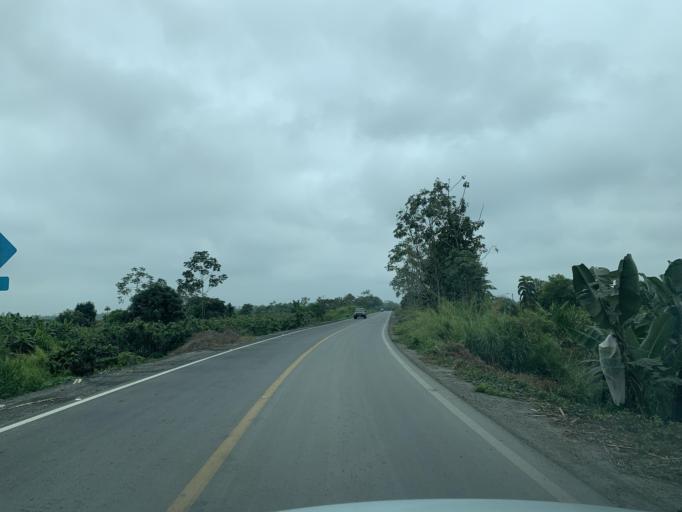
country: EC
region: Guayas
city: Coronel Marcelino Mariduena
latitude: -2.3039
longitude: -79.5014
